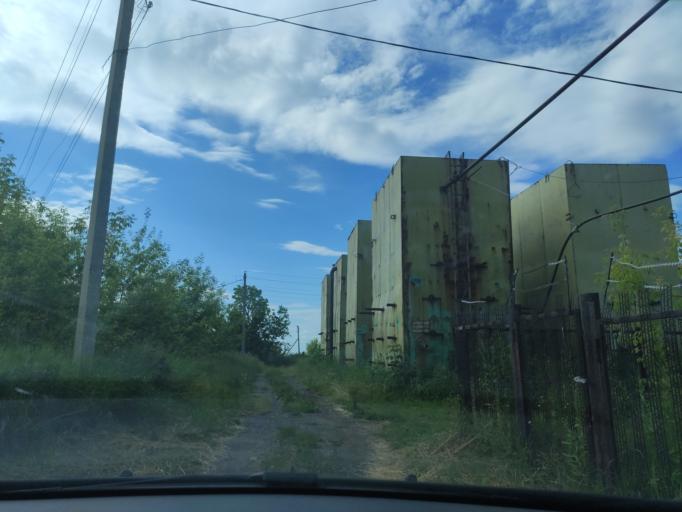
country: RU
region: Ulyanovsk
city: Cherdakly
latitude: 54.4431
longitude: 48.8955
